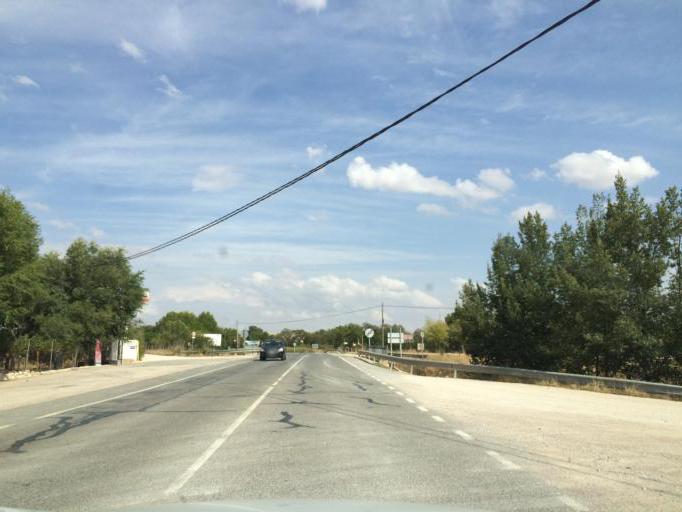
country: ES
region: Castille-La Mancha
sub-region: Provincia de Albacete
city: Albacete
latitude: 38.9972
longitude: -1.8908
